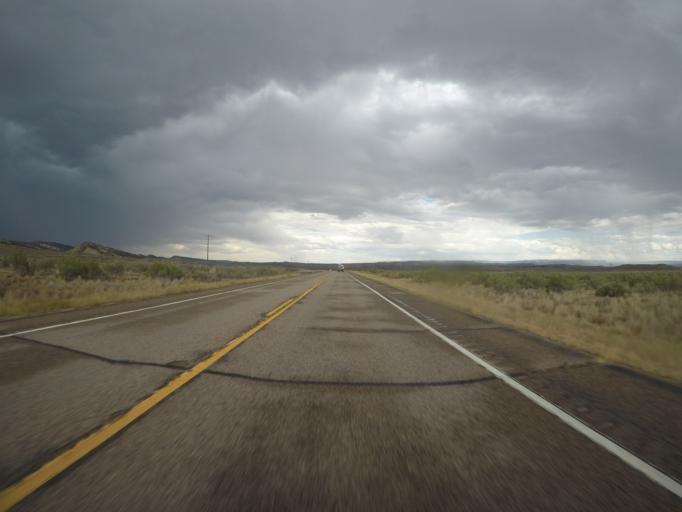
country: US
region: Colorado
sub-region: Rio Blanco County
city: Rangely
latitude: 40.2381
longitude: -108.9134
